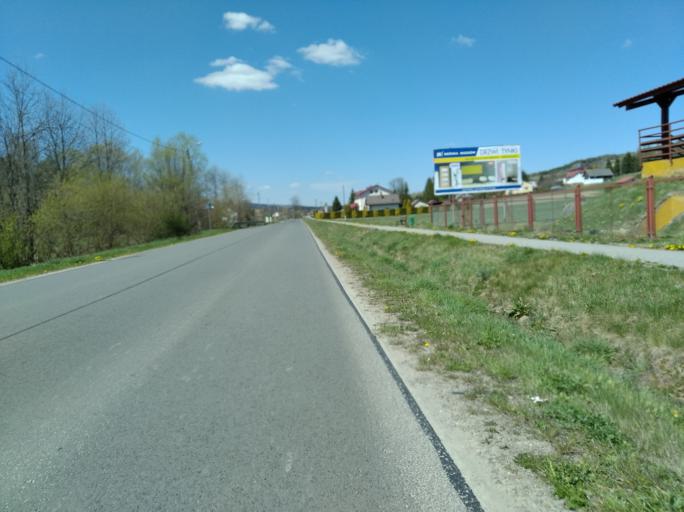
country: PL
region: Subcarpathian Voivodeship
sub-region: Powiat brzozowski
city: Dydnia
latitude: 49.6860
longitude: 22.1724
